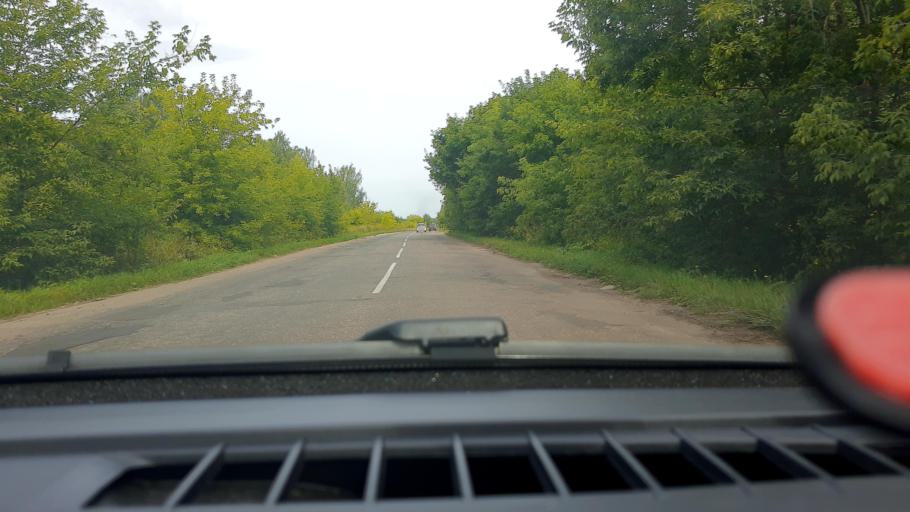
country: RU
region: Nizjnij Novgorod
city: Bogorodsk
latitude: 56.0733
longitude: 43.5773
